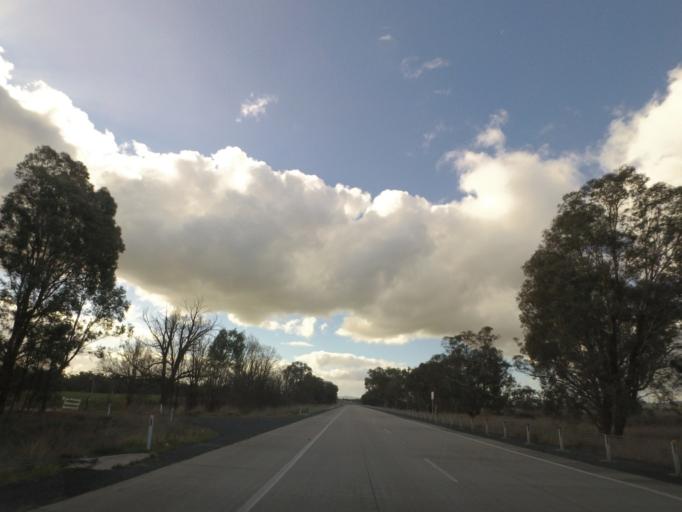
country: AU
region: New South Wales
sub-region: Greater Hume Shire
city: Holbrook
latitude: -35.7429
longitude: 147.3015
